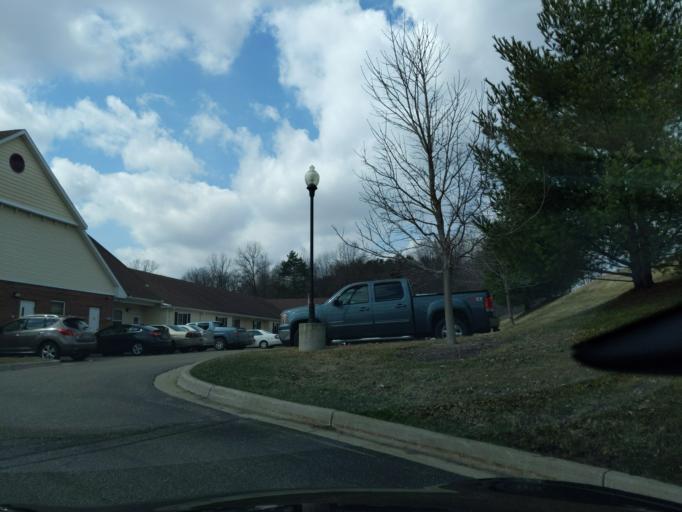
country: US
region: Michigan
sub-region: Calhoun County
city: Lakeview
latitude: 42.2528
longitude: -85.1989
